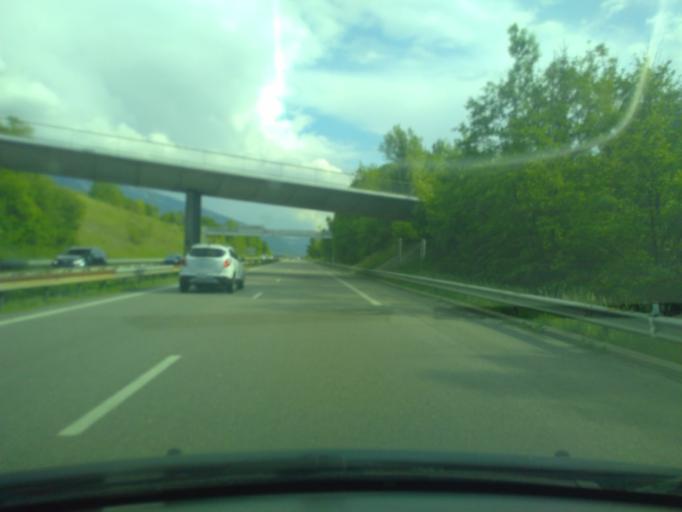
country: FR
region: Rhone-Alpes
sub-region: Departement de la Haute-Savoie
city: Chavanod
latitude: 45.8567
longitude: 6.0563
